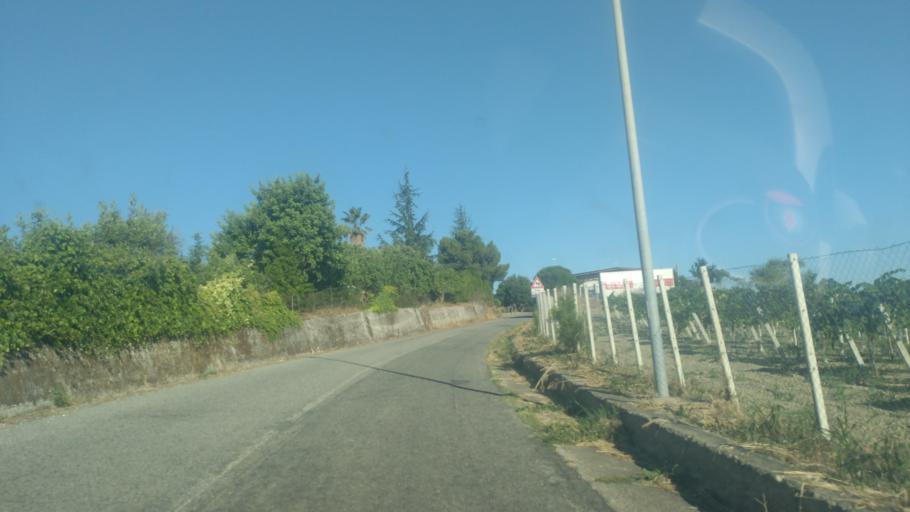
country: IT
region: Calabria
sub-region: Provincia di Catanzaro
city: Staletti
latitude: 38.7666
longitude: 16.5284
